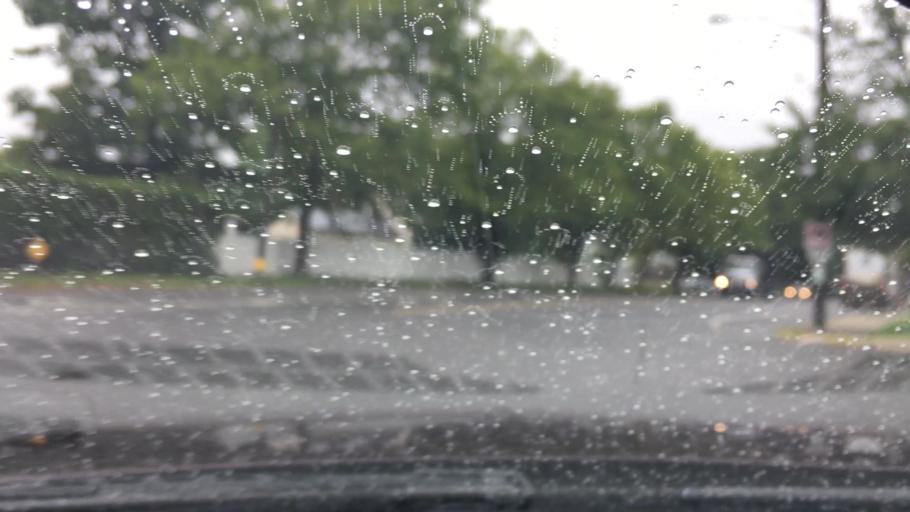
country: US
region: New York
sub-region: Nassau County
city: Old Bethpage
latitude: 40.7630
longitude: -73.4535
